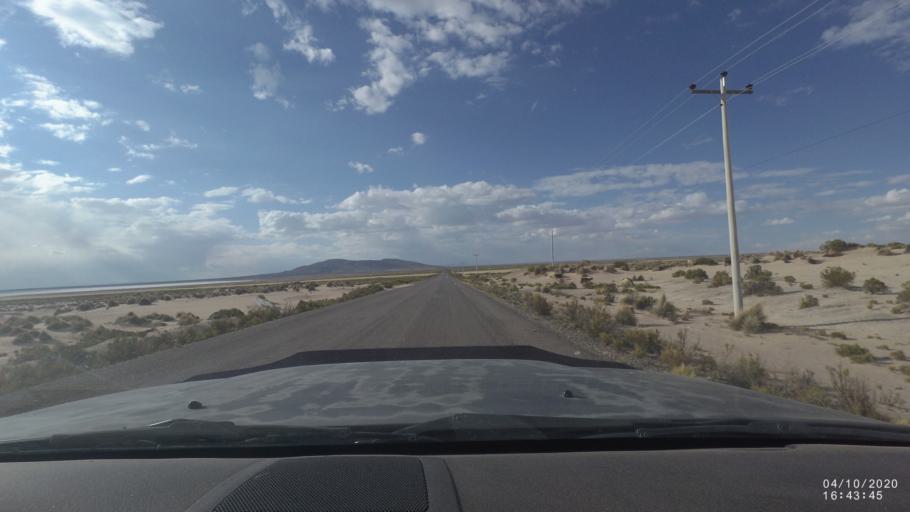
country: BO
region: Oruro
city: Poopo
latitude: -18.6920
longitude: -67.5573
